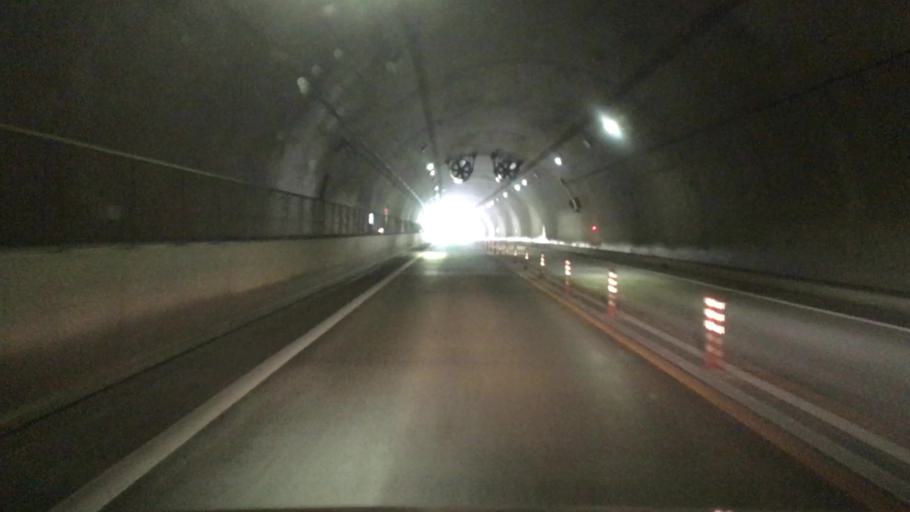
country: JP
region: Hyogo
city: Toyooka
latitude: 35.6294
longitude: 134.5244
